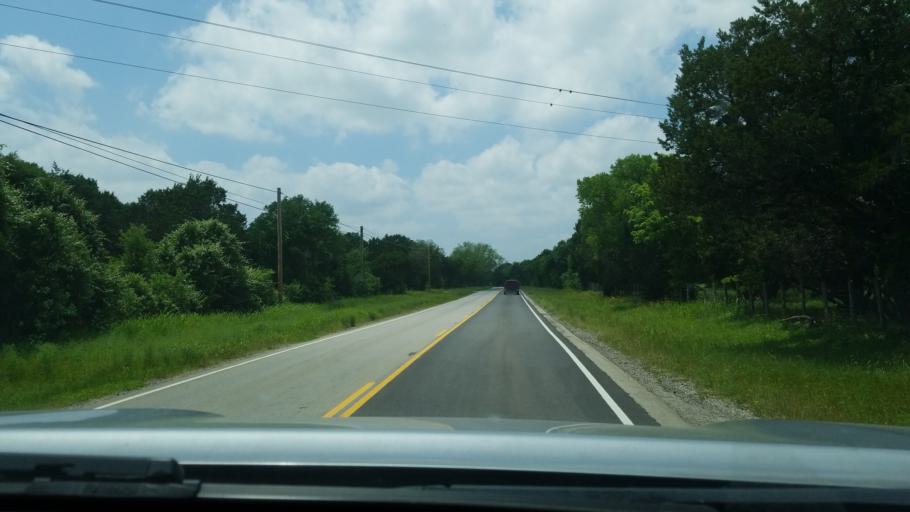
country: US
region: Texas
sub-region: Hays County
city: Dripping Springs
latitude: 30.1453
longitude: -98.0414
